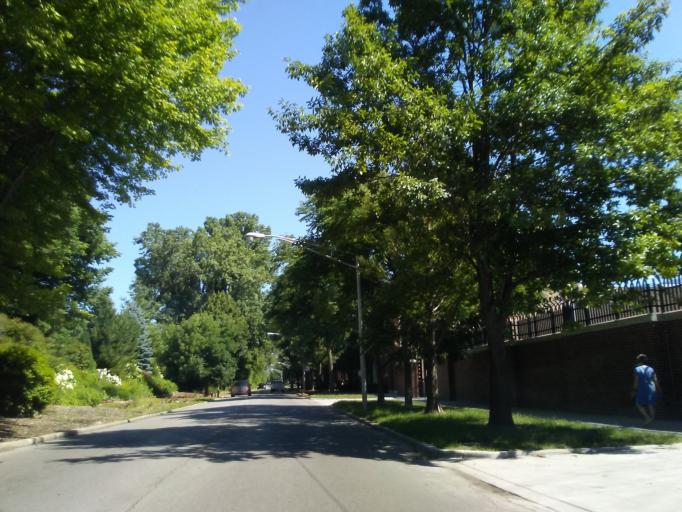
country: US
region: Illinois
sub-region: Cook County
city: Evanston
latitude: 41.9869
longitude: -87.6746
